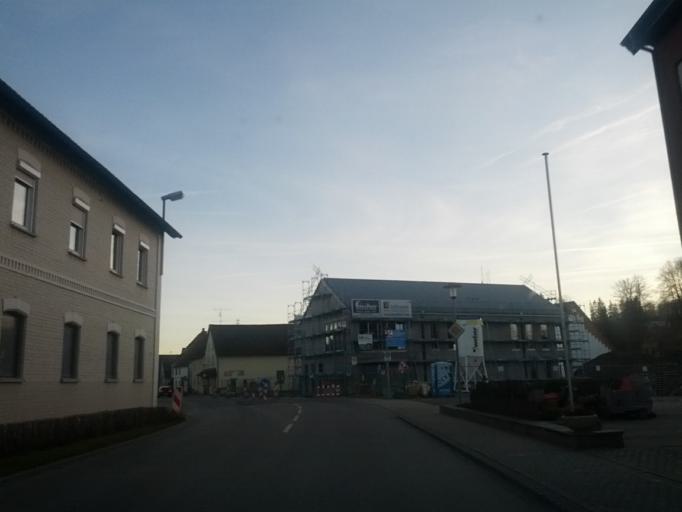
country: DE
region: Baden-Wuerttemberg
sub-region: Tuebingen Region
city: Berkheim
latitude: 48.0428
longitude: 10.0820
